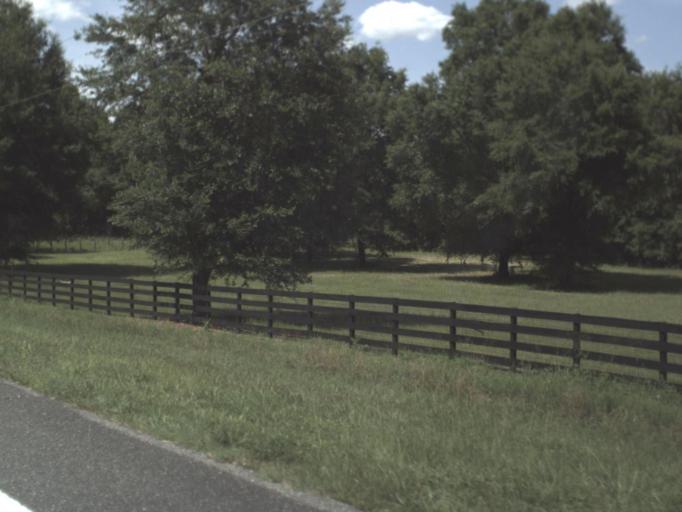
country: US
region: Florida
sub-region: Alachua County
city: High Springs
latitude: 29.7817
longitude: -82.7408
